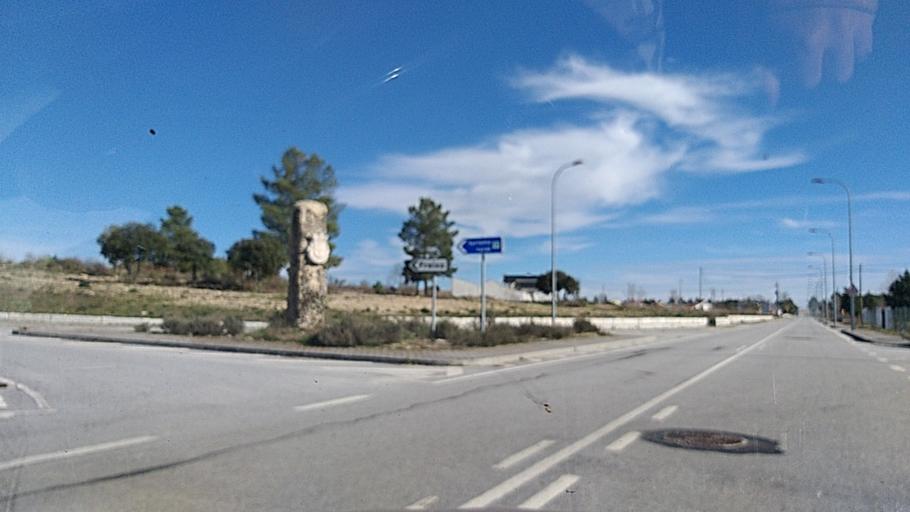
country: PT
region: Guarda
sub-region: Pinhel
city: Pinhel
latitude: 40.6034
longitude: -7.0022
